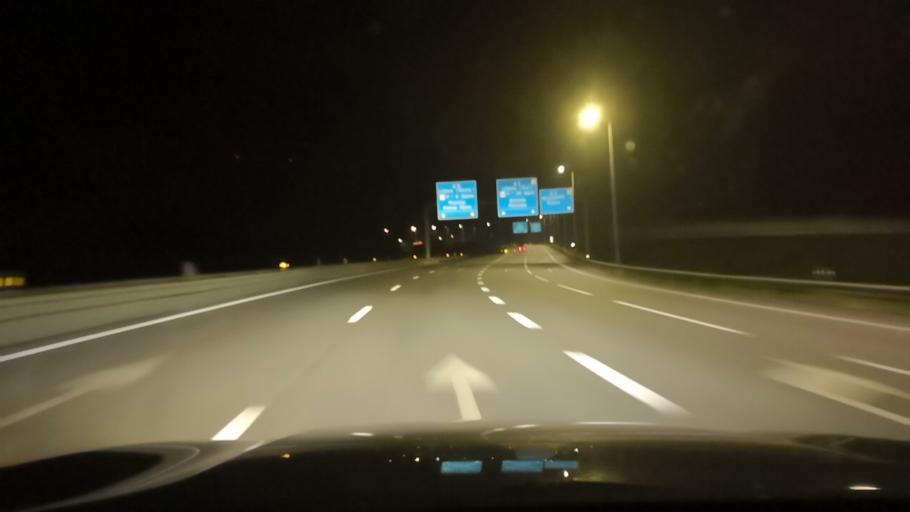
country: PT
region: Setubal
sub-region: Palmela
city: Palmela
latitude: 38.5765
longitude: -8.8657
